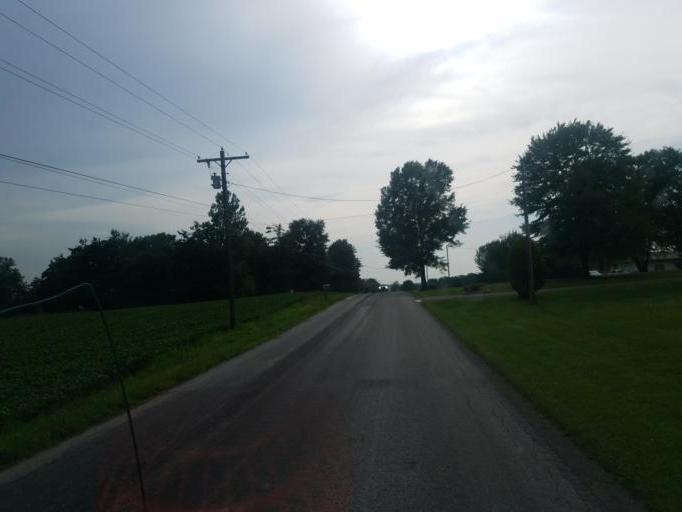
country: US
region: Ohio
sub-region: Wayne County
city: West Salem
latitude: 40.9009
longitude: -82.1007
